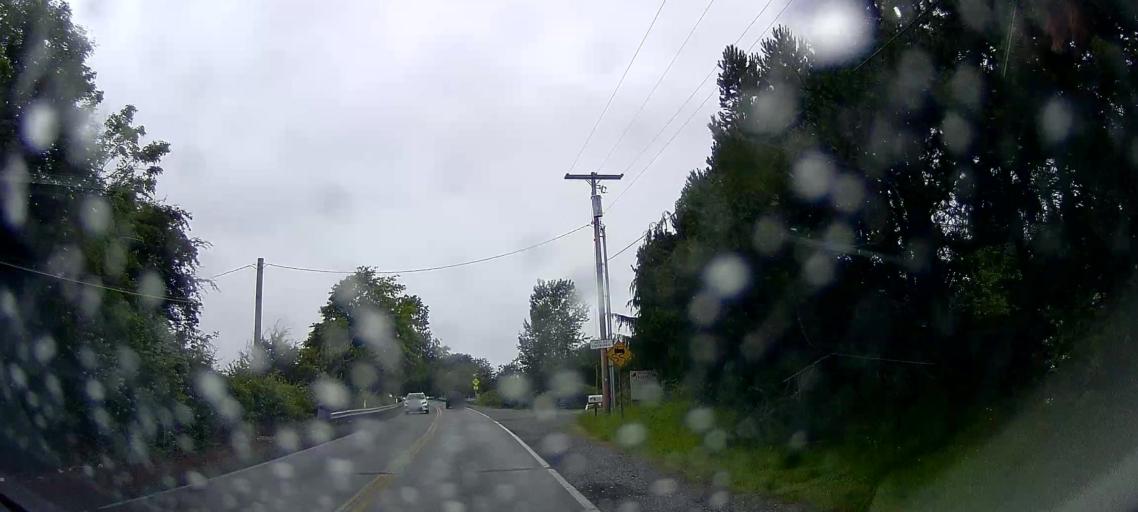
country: US
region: Washington
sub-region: Whatcom County
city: Marietta-Alderwood
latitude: 48.7823
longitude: -122.5449
